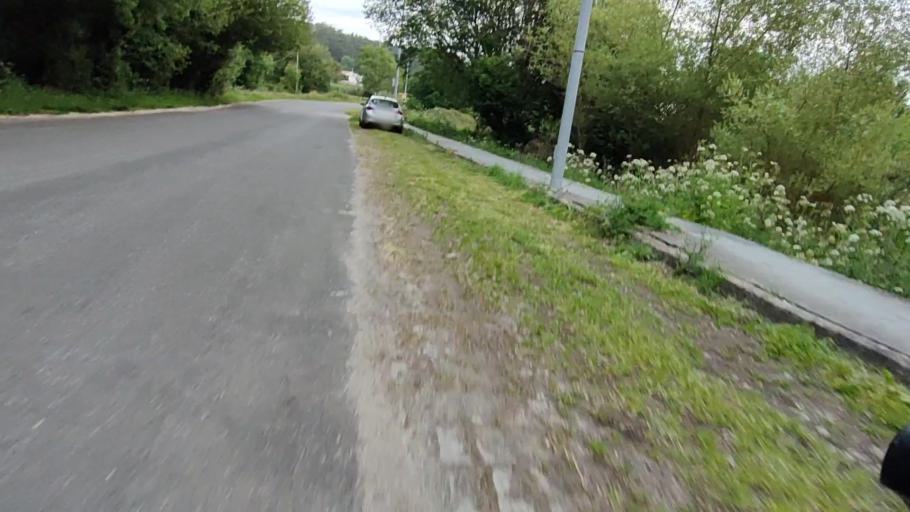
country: ES
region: Galicia
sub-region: Provincia da Coruna
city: Boiro
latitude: 42.6139
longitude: -8.8735
